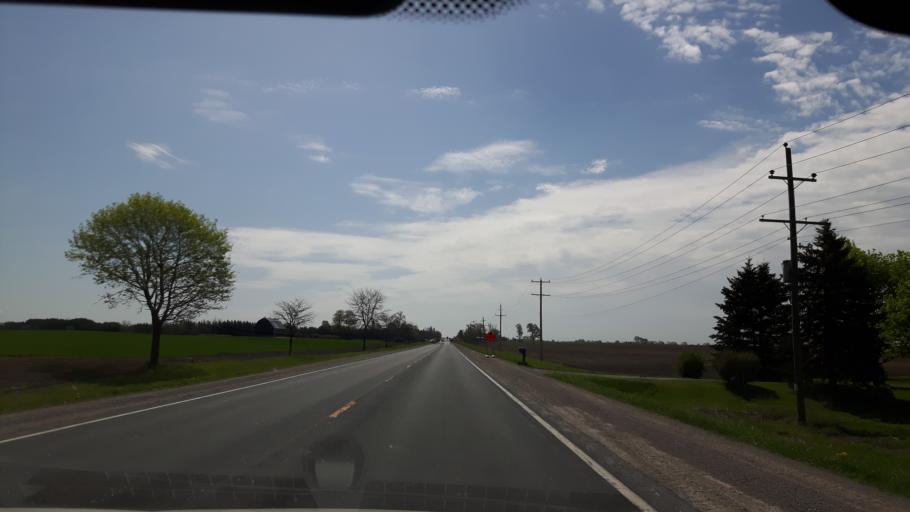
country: CA
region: Ontario
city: South Huron
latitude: 43.1793
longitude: -81.3838
